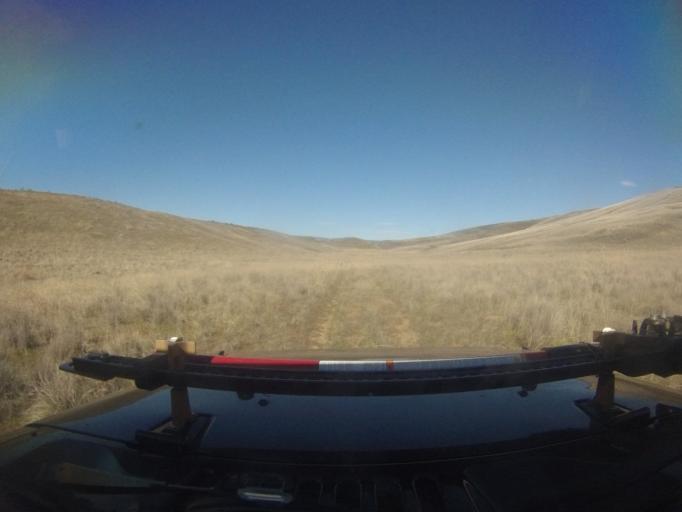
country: US
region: Washington
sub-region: Grant County
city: Quincy
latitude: 47.2385
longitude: -119.9861
